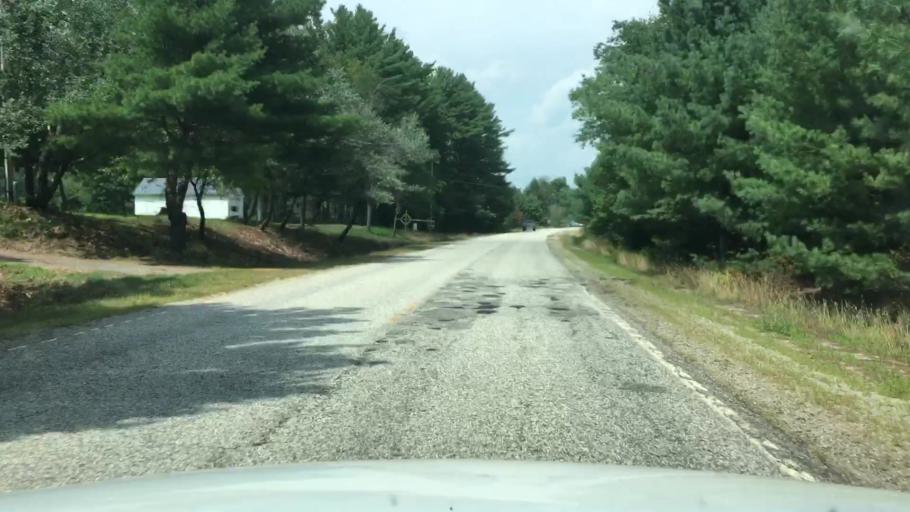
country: US
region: Maine
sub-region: Oxford County
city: Rumford
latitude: 44.5904
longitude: -70.7366
